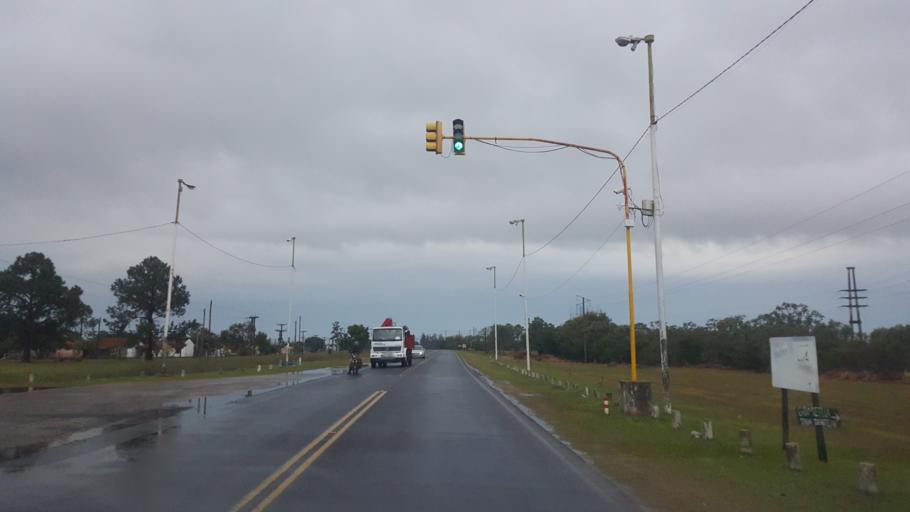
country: AR
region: Corrientes
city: Ituzaingo
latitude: -27.5723
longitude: -56.6696
